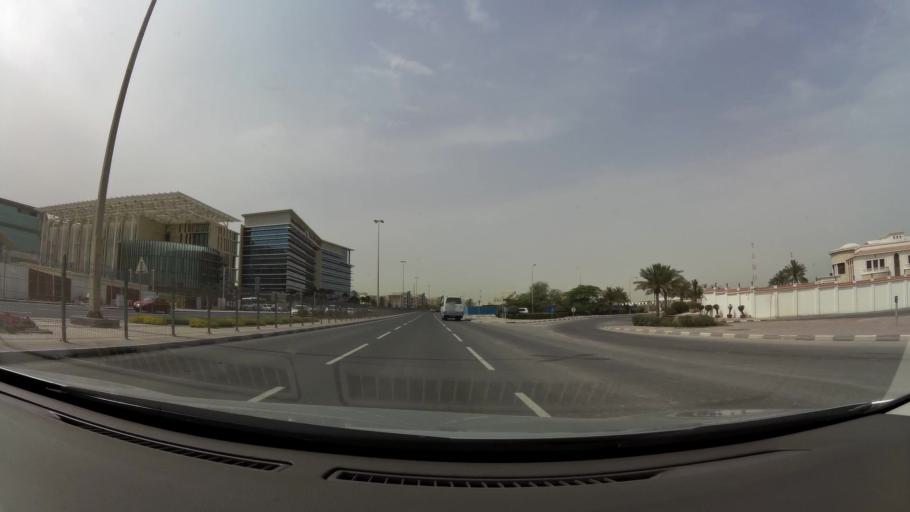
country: QA
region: Baladiyat ad Dawhah
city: Doha
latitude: 25.2957
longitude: 51.5110
